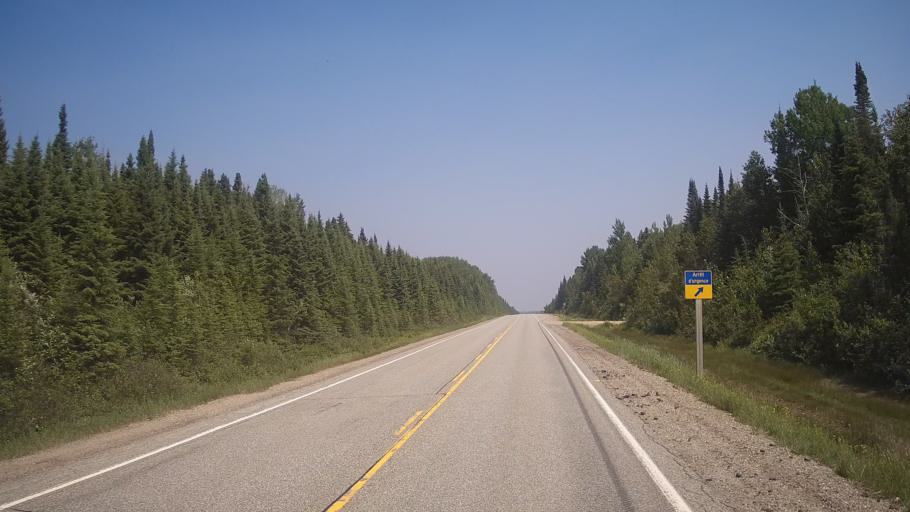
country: CA
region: Ontario
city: Timmins
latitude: 48.2000
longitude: -81.5797
